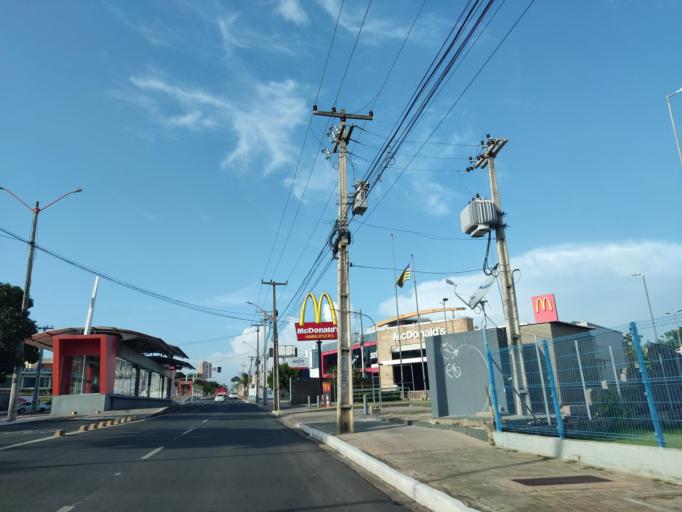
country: BR
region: Piaui
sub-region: Teresina
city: Teresina
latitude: -5.0739
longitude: -42.7727
